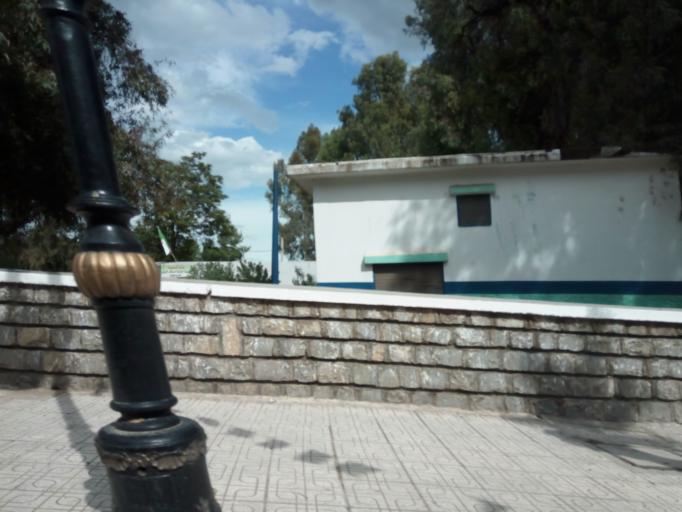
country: DZ
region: Constantine
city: Constantine
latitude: 36.3544
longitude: 6.6094
